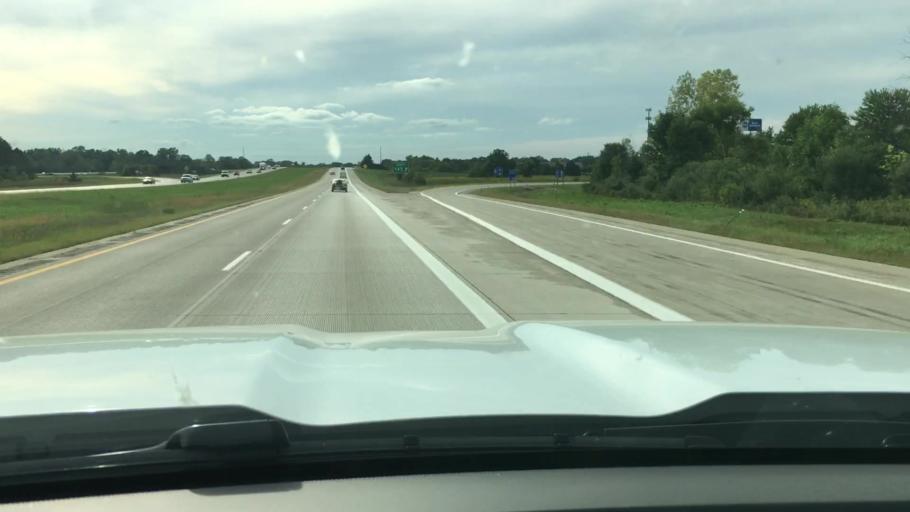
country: US
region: Michigan
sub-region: Genesee County
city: Davison
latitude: 43.0123
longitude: -83.5108
